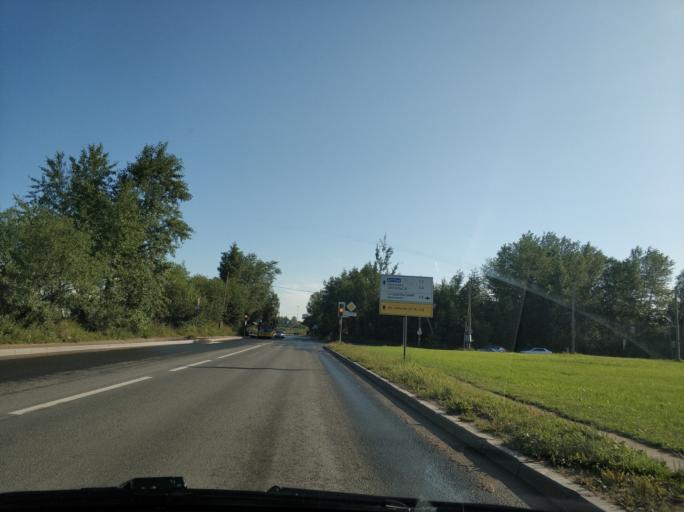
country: RU
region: Leningrad
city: Bugry
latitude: 60.0573
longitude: 30.3834
